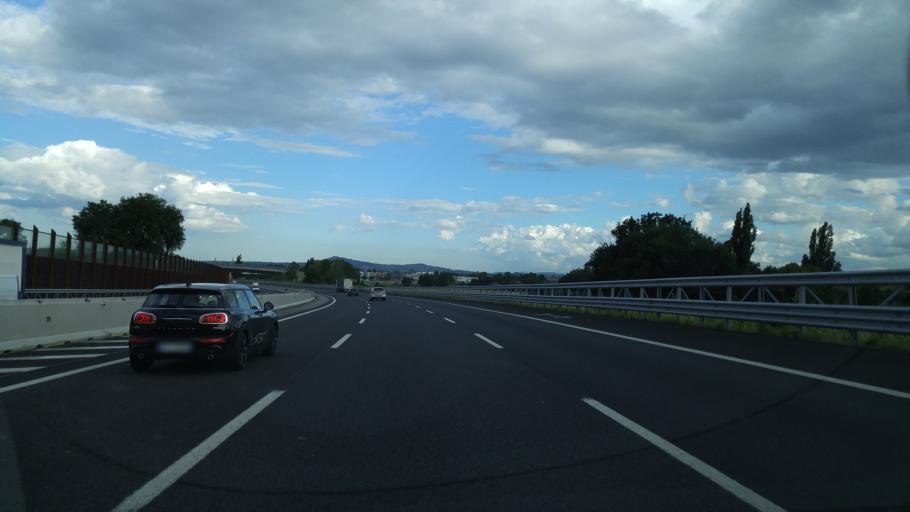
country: IT
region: Emilia-Romagna
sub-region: Provincia di Rimini
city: Santa Monica-Cella
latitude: 43.9714
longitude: 12.6661
